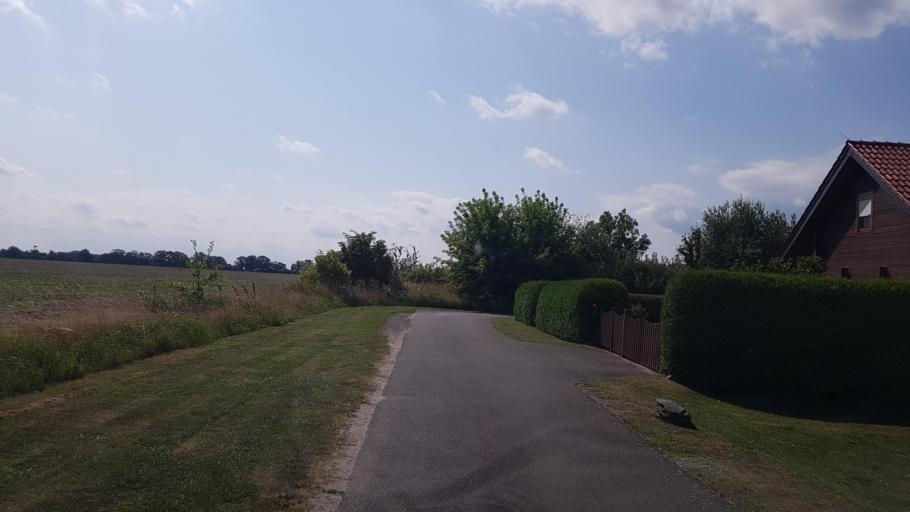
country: DE
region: Brandenburg
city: Sonnewalde
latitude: 51.6944
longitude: 13.6534
